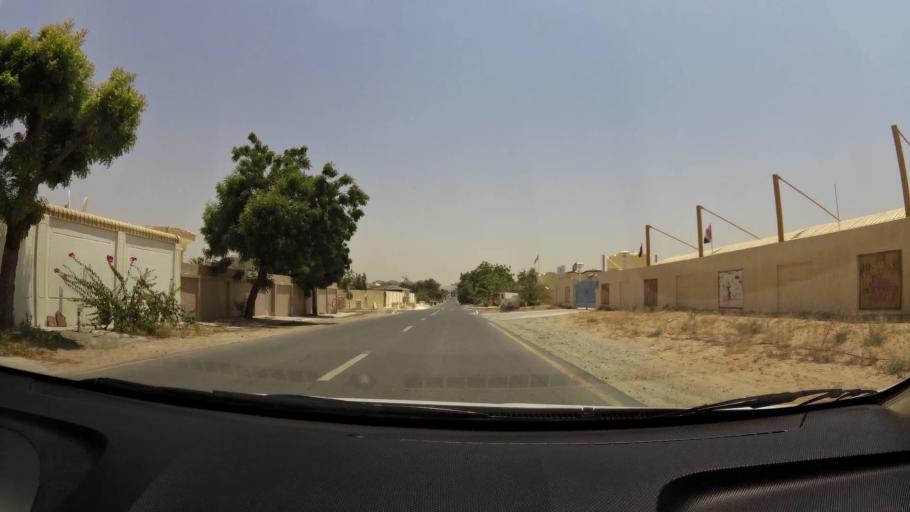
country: AE
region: Ajman
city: Ajman
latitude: 25.4219
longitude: 55.5057
